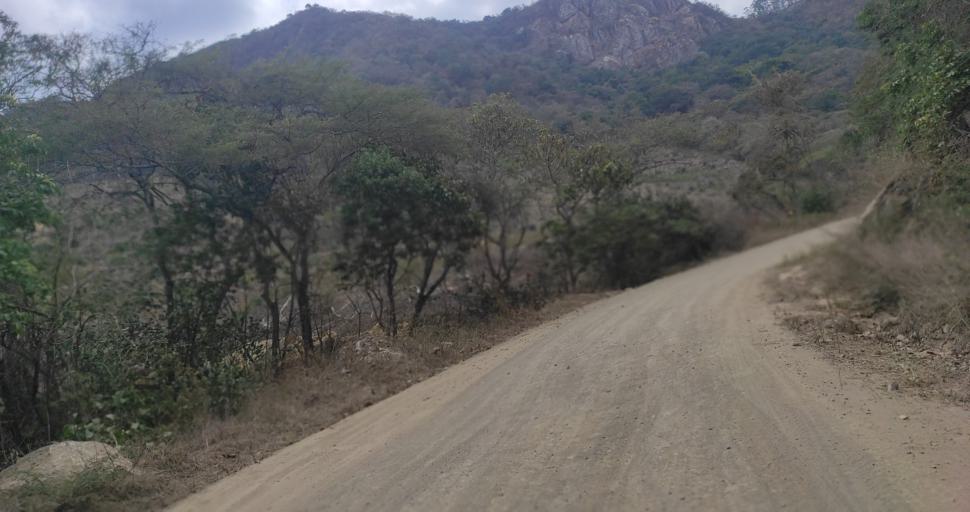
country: EC
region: Loja
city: Catacocha
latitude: -4.0287
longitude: -79.6422
